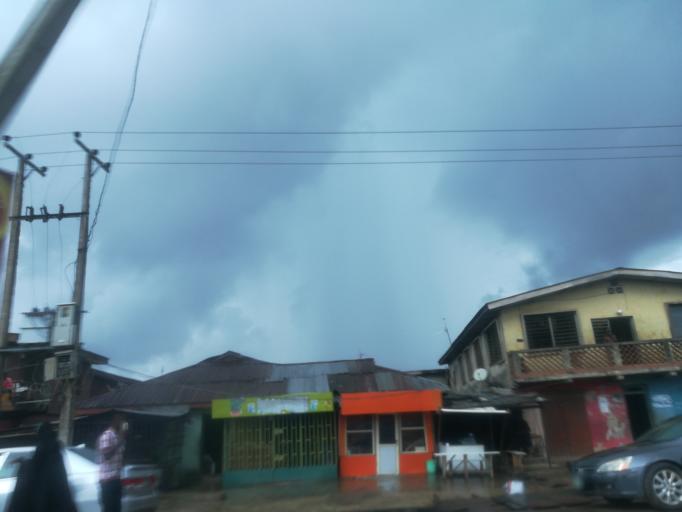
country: NG
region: Lagos
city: Agege
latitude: 6.6203
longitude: 3.3202
